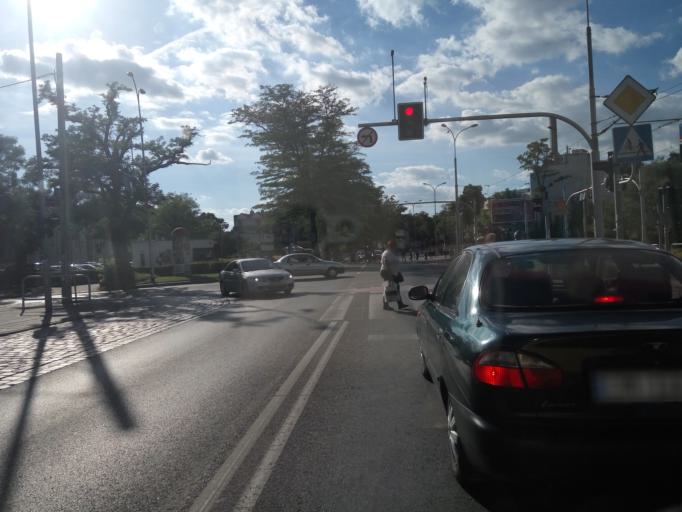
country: PL
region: Lower Silesian Voivodeship
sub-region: Powiat wroclawski
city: Wroclaw
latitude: 51.1401
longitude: 16.9594
